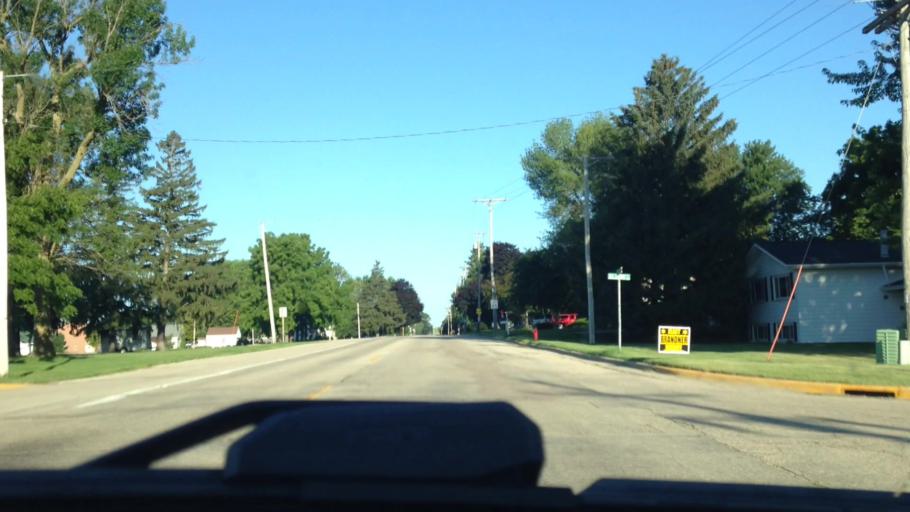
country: US
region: Wisconsin
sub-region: Columbia County
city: Poynette
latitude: 43.3375
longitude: -89.3726
